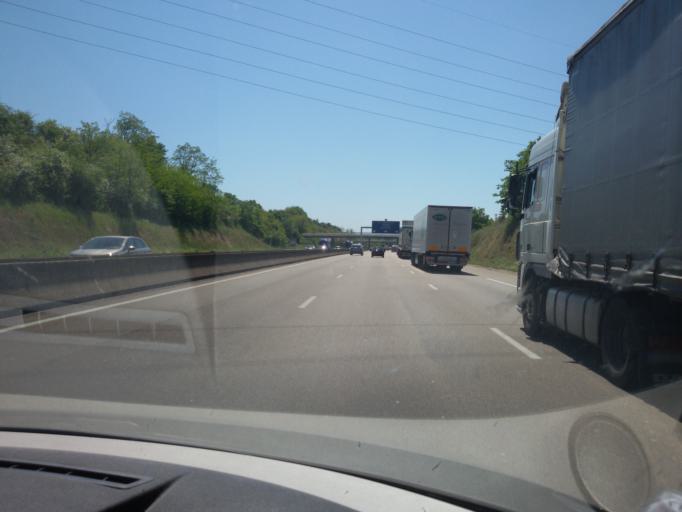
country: FR
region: Rhone-Alpes
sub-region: Departement de l'Isere
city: Chanas
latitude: 45.3285
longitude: 4.8115
